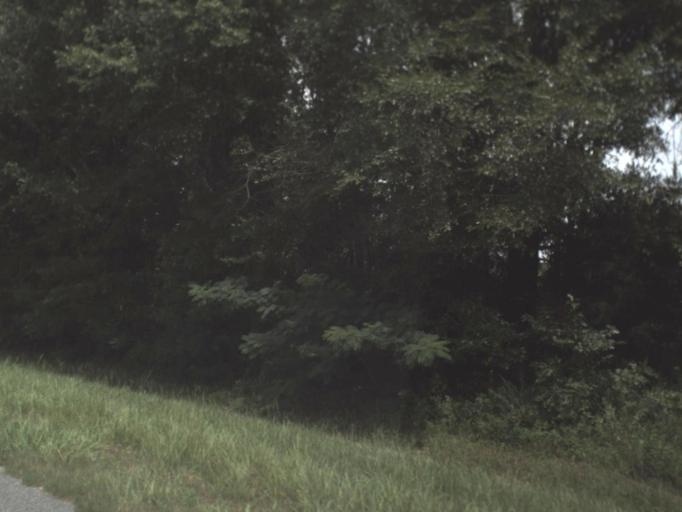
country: US
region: Florida
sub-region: Madison County
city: Madison
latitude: 30.4909
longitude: -83.3851
